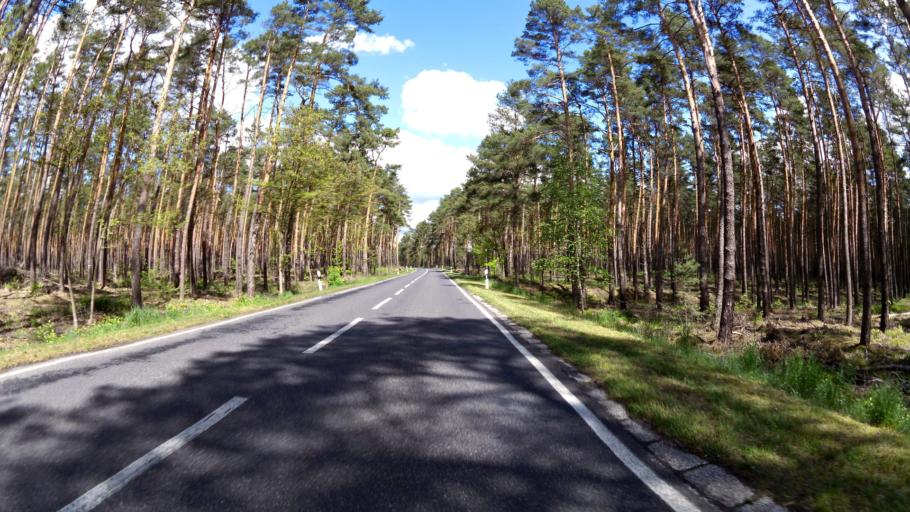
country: DE
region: Brandenburg
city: Wendisch Rietz
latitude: 52.1382
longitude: 13.9652
